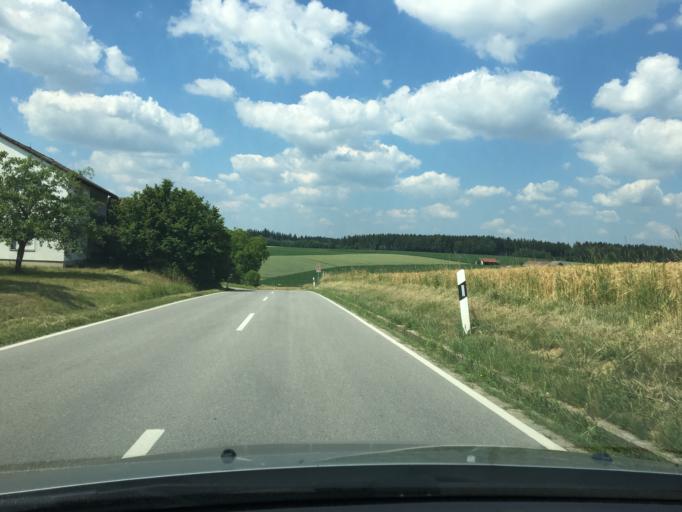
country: DE
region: Bavaria
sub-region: Upper Bavaria
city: Neumarkt-Sankt Veit
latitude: 48.3777
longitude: 12.5066
